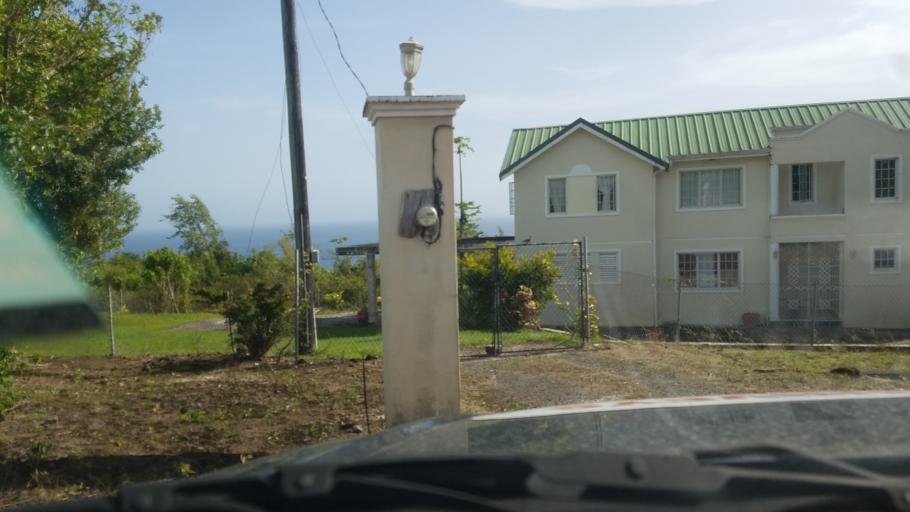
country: LC
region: Anse-la-Raye
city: Anse La Raye
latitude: 13.9475
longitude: -61.0339
